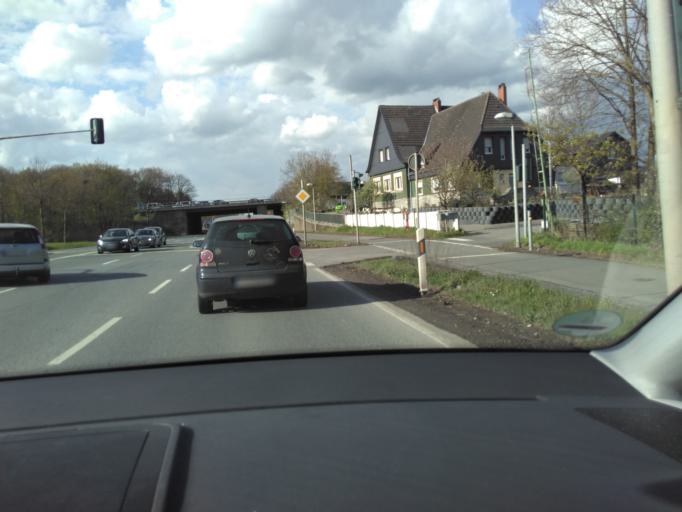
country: DE
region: North Rhine-Westphalia
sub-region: Regierungsbezirk Munster
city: Beckum
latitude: 51.7780
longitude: 8.0333
